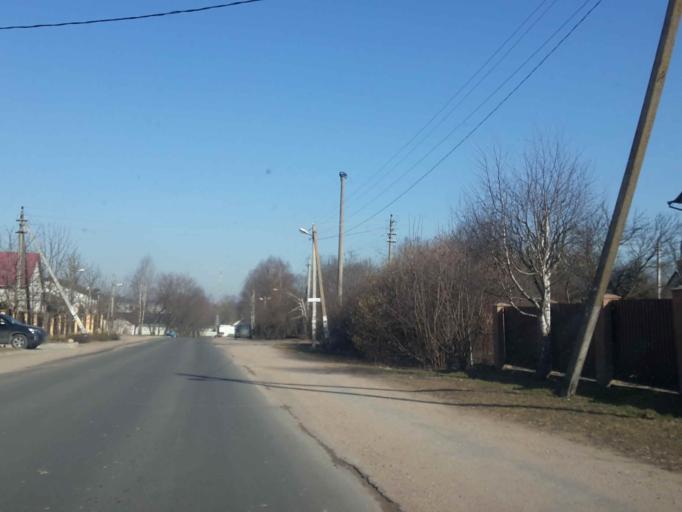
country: BY
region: Minsk
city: Zhdanovichy
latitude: 53.9193
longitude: 27.3901
